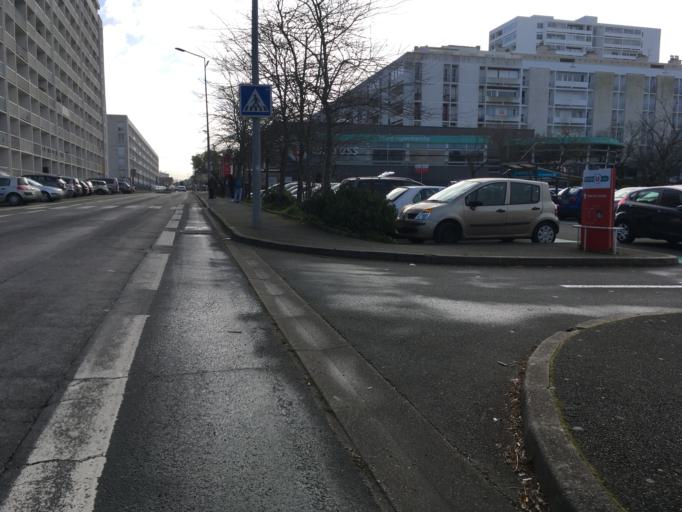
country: FR
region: Poitou-Charentes
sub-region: Departement de la Charente-Maritime
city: La Rochelle
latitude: 46.1676
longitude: -1.1812
